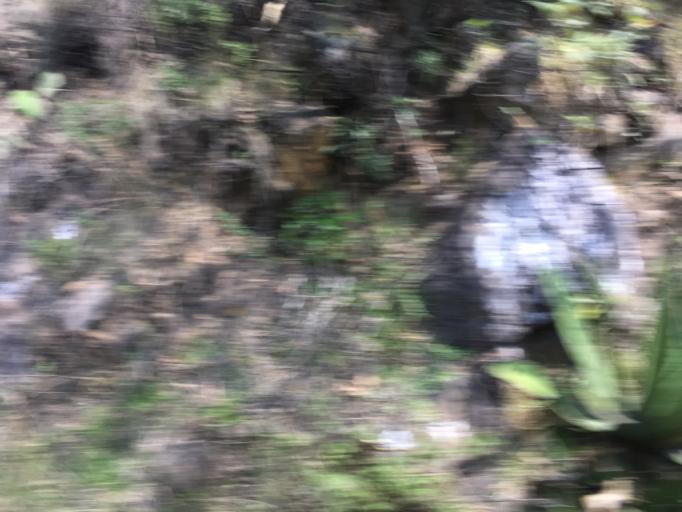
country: MX
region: Mexico
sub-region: Morelos
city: San Marcos Tlazalpan
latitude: 19.7851
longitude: -99.7317
